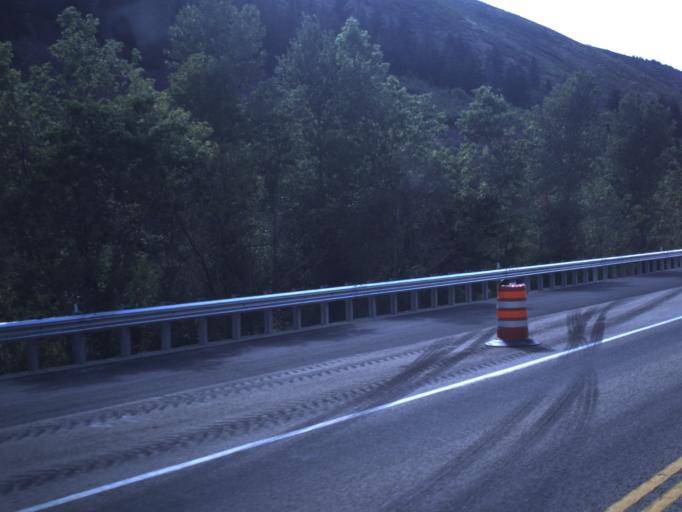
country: US
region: Utah
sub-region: Wasatch County
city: Heber
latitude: 40.4143
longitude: -111.3294
